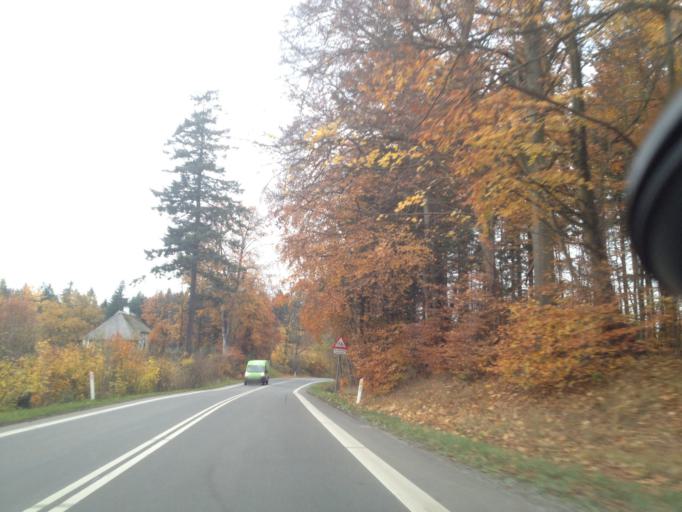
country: DK
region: South Denmark
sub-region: Nordfyns Kommune
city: Sonderso
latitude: 55.4394
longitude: 10.2143
